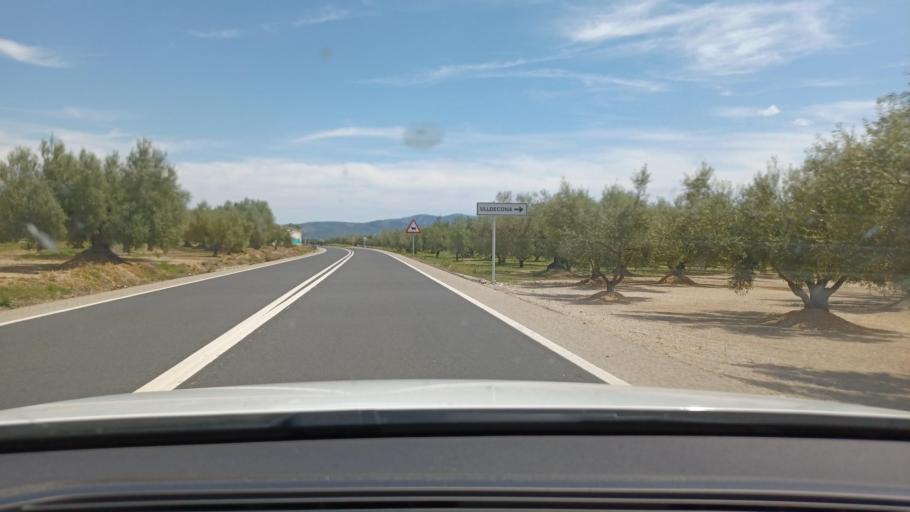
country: ES
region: Catalonia
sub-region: Provincia de Tarragona
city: Ulldecona
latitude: 40.6414
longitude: 0.3699
